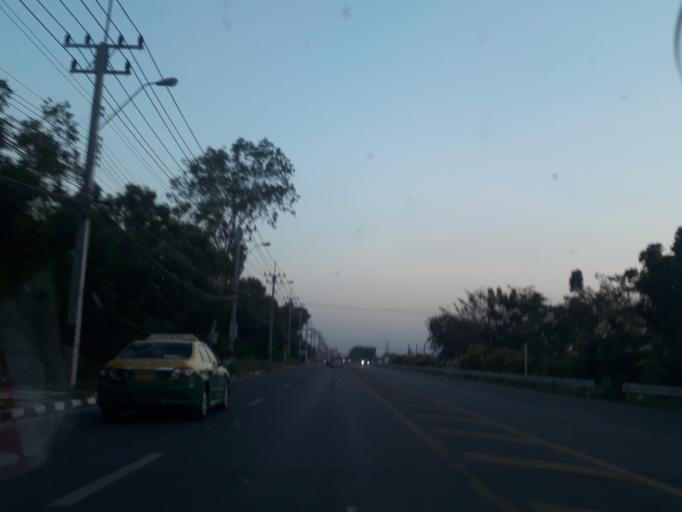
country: TH
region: Pathum Thani
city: Thanyaburi
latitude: 14.0804
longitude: 100.7103
